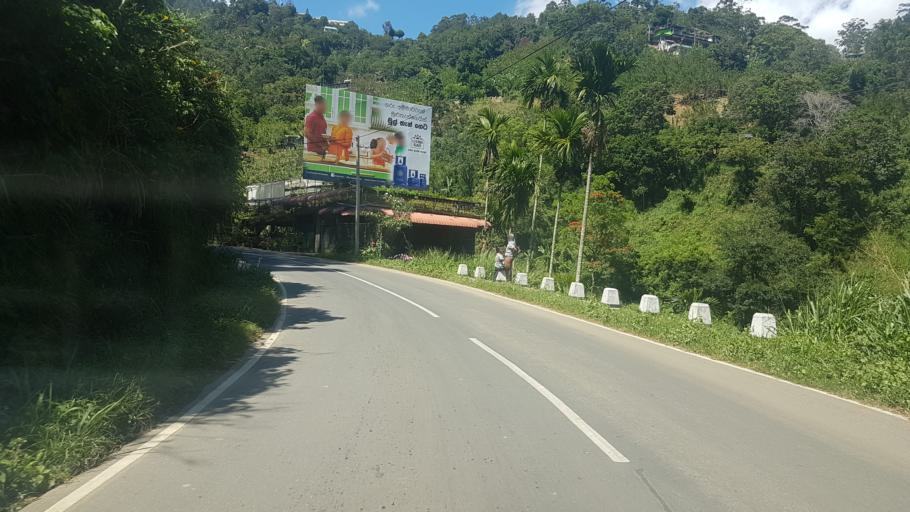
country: LK
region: Uva
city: Badulla
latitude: 6.8674
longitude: 81.0487
